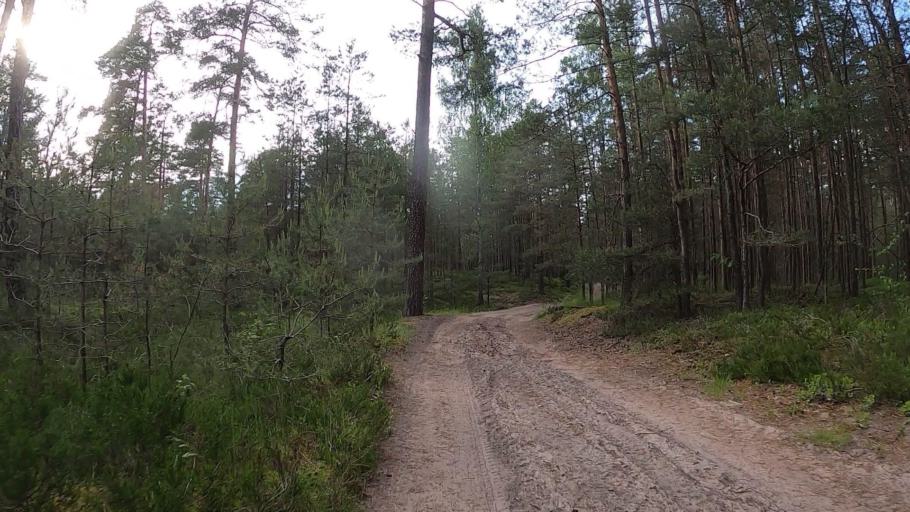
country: LV
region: Riga
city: Jaunciems
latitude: 57.0741
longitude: 24.1320
